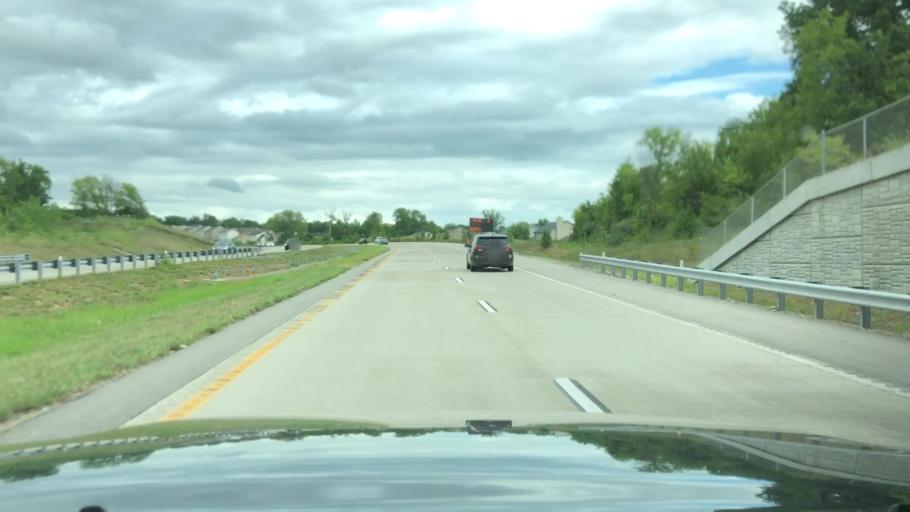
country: US
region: Missouri
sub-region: Saint Charles County
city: Cottleville
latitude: 38.7347
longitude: -90.6659
